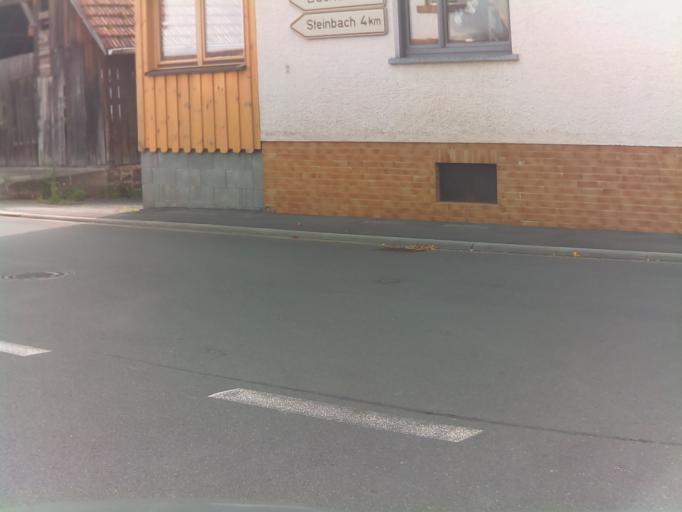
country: DE
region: Baden-Wuerttemberg
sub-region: Karlsruhe Region
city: Mudau
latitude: 49.5801
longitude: 9.2642
